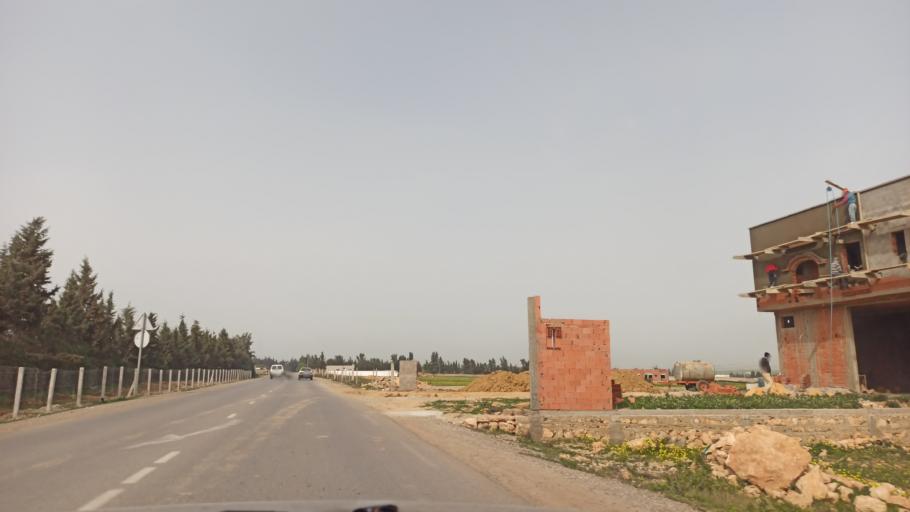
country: TN
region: Zaghwan
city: Zaghouan
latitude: 36.4191
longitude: 10.1032
